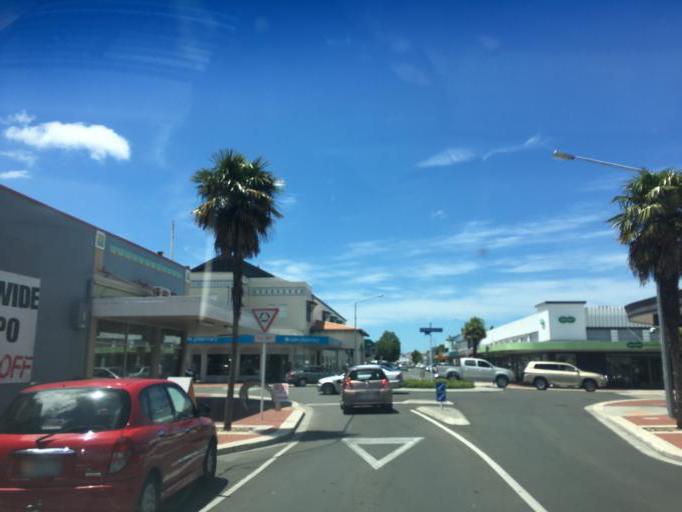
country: NZ
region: Hawke's Bay
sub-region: Hastings District
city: Hastings
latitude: -39.6404
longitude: 176.8410
